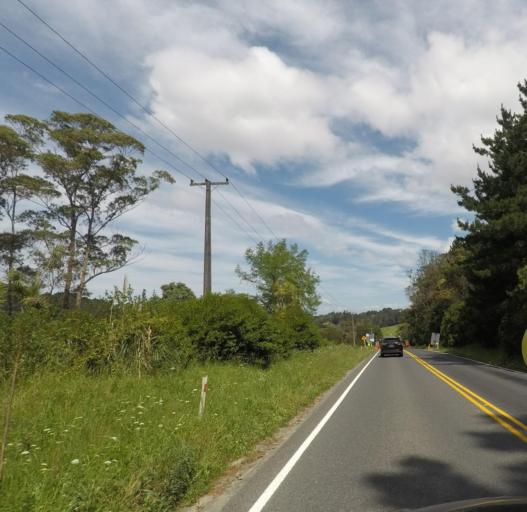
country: NZ
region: Auckland
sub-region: Auckland
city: Rothesay Bay
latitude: -36.6727
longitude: 174.6851
